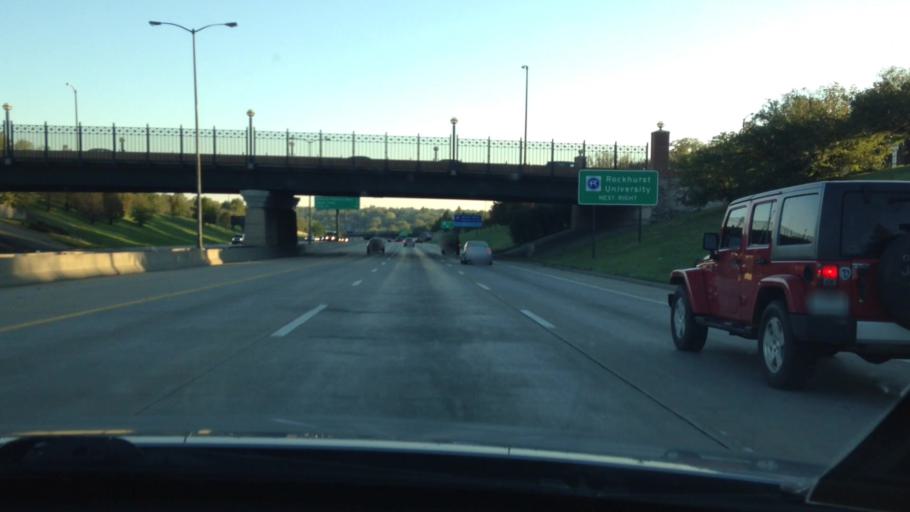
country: US
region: Missouri
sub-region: Jackson County
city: Kansas City
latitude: 39.0564
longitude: -94.5614
